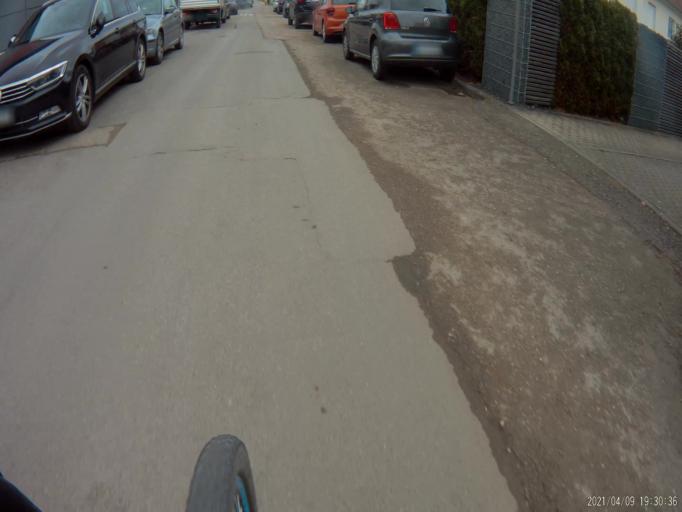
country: DE
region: Baden-Wuerttemberg
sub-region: Regierungsbezirk Stuttgart
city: Neuhausen auf den Fildern
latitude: 48.6802
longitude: 9.2873
